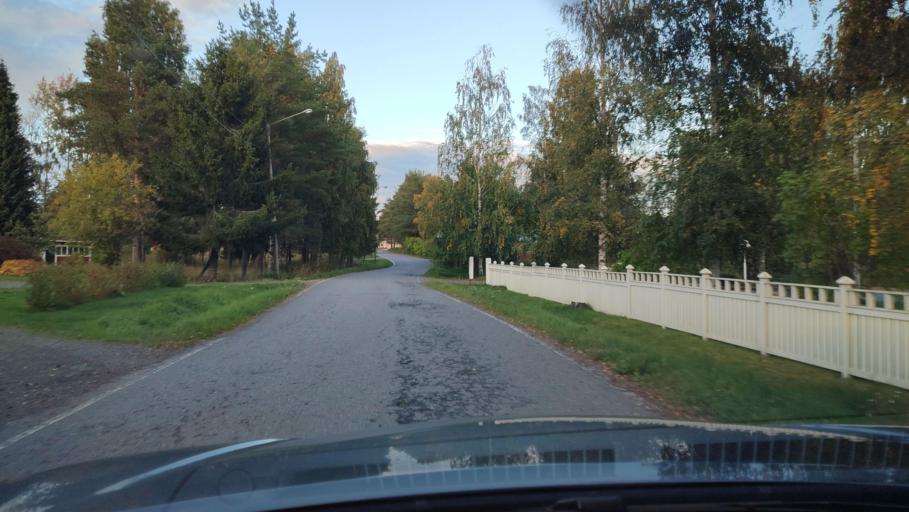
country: FI
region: Ostrobothnia
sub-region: Sydosterbotten
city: Kristinestad
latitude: 62.2437
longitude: 21.5172
